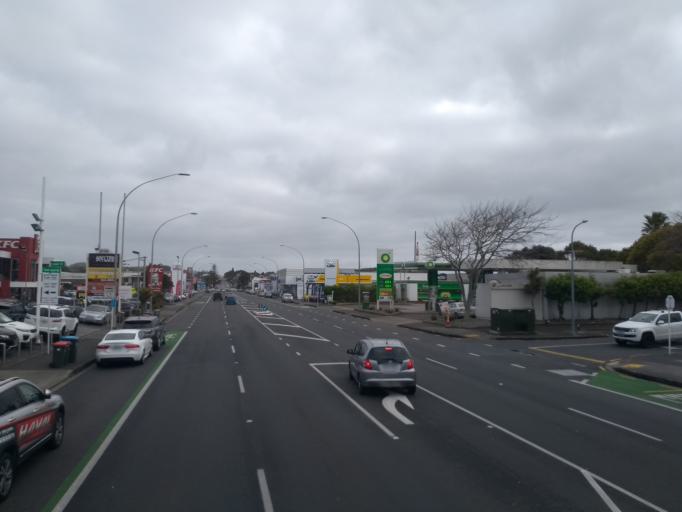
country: NZ
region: Auckland
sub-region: Auckland
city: Auckland
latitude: -36.8929
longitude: 174.7974
